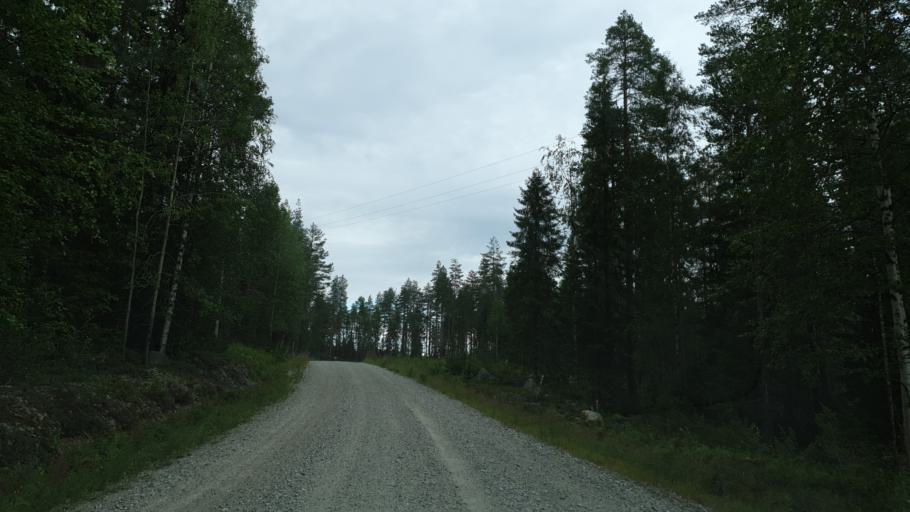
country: FI
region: Kainuu
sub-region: Kehys-Kainuu
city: Kuhmo
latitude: 64.4541
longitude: 29.5758
